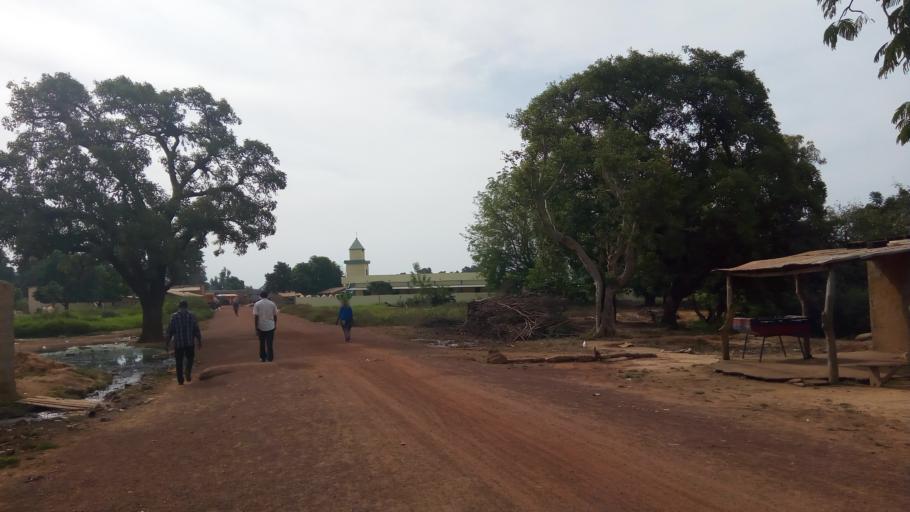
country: ML
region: Koulikoro
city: Kangaba
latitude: 11.6889
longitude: -8.6958
